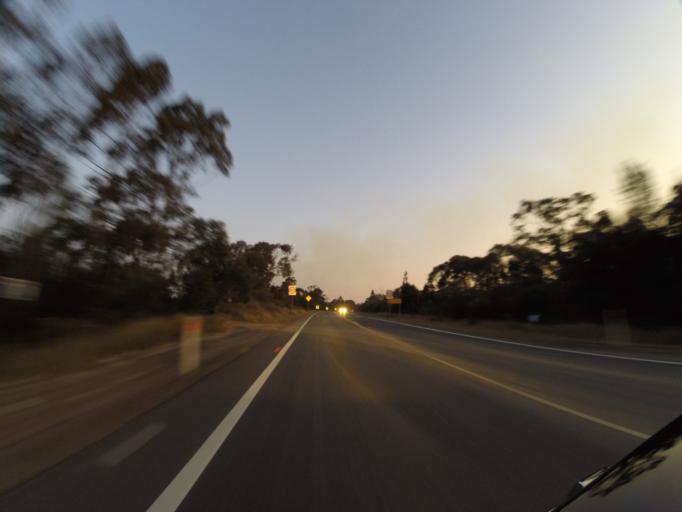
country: AU
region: New South Wales
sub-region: Sutherland Shire
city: Menai
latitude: -33.9994
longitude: 150.9959
